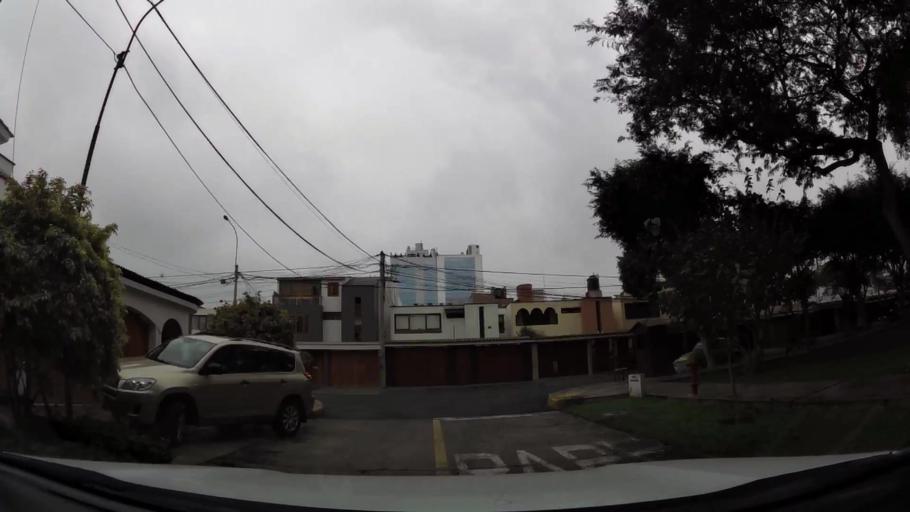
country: PE
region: Lima
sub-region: Lima
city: Surco
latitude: -12.1293
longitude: -77.0048
